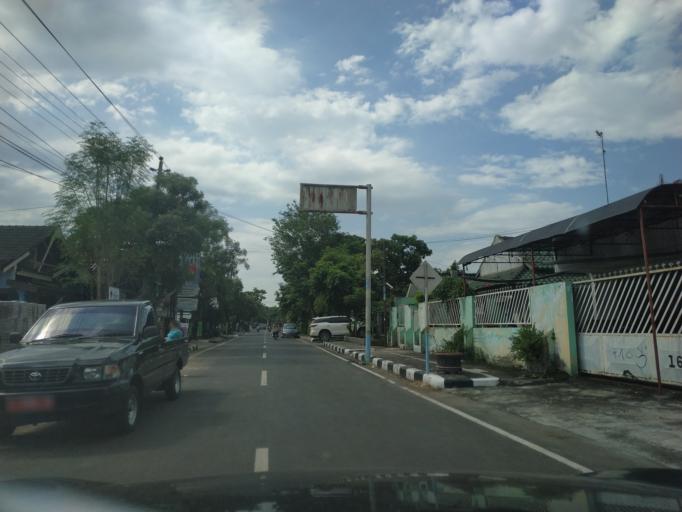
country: ID
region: Central Java
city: Pati
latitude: -6.7567
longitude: 111.0326
